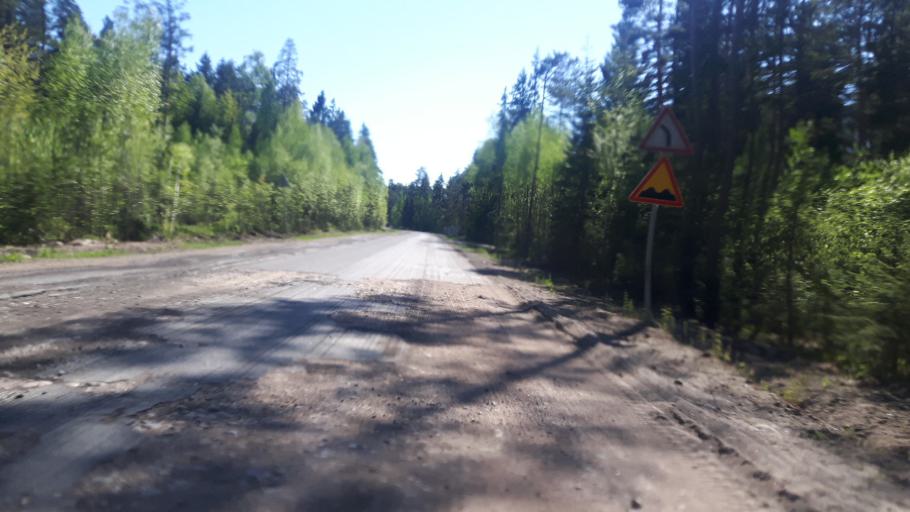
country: RU
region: Leningrad
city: Sosnovyy Bor
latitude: 60.2363
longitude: 29.0023
